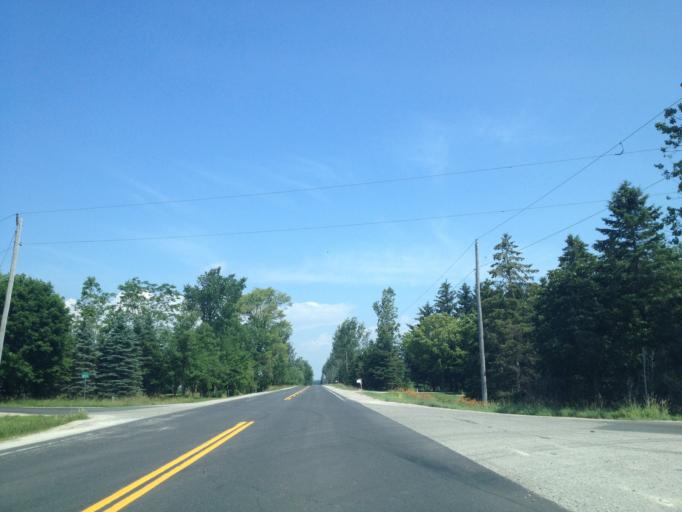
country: CA
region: Ontario
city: Huron East
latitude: 43.4129
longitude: -81.2211
